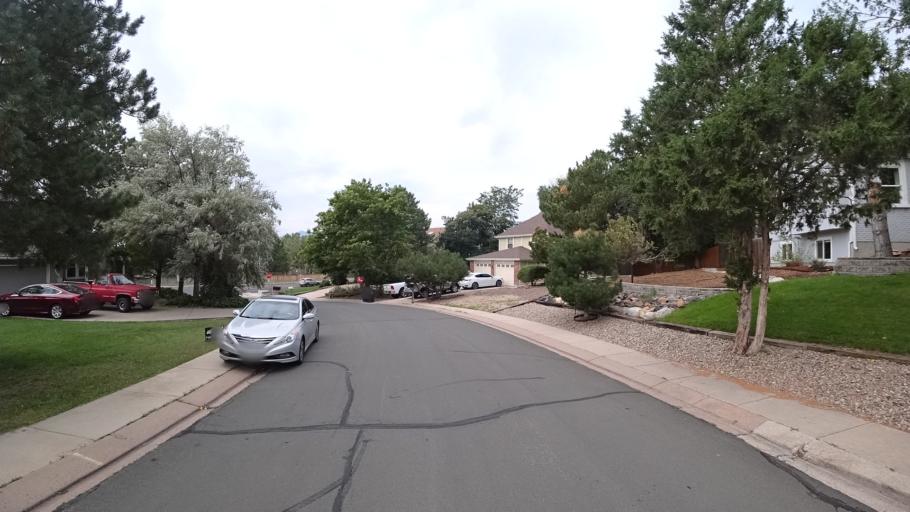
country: US
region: Colorado
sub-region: El Paso County
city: Air Force Academy
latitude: 38.9262
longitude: -104.8401
